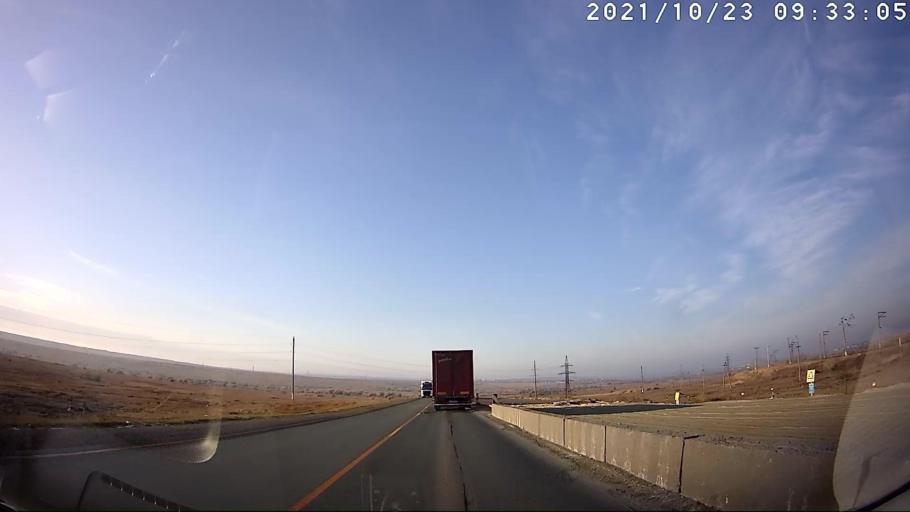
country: RU
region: Saratov
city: Sokolovyy
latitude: 51.6648
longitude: 45.8542
